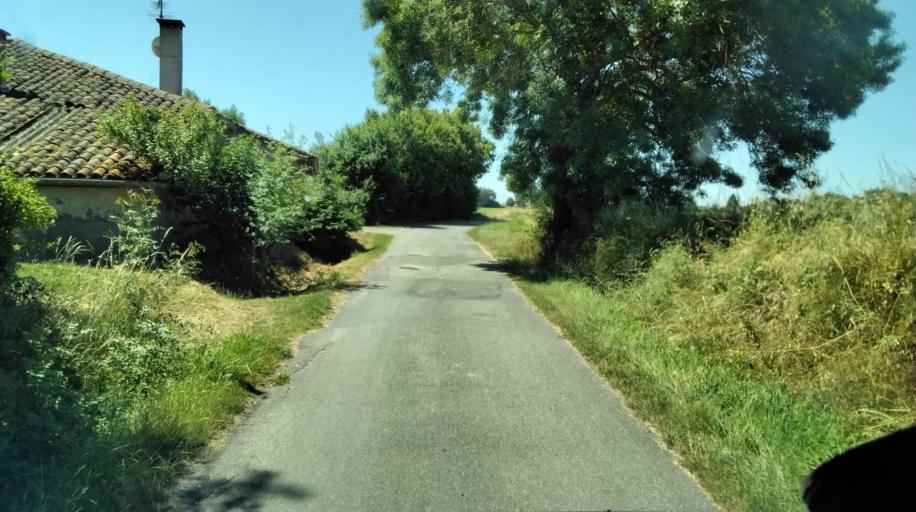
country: FR
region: Midi-Pyrenees
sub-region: Departement de la Haute-Garonne
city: Sainte-Foy-de-Peyrolieres
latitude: 43.4833
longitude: 1.1312
